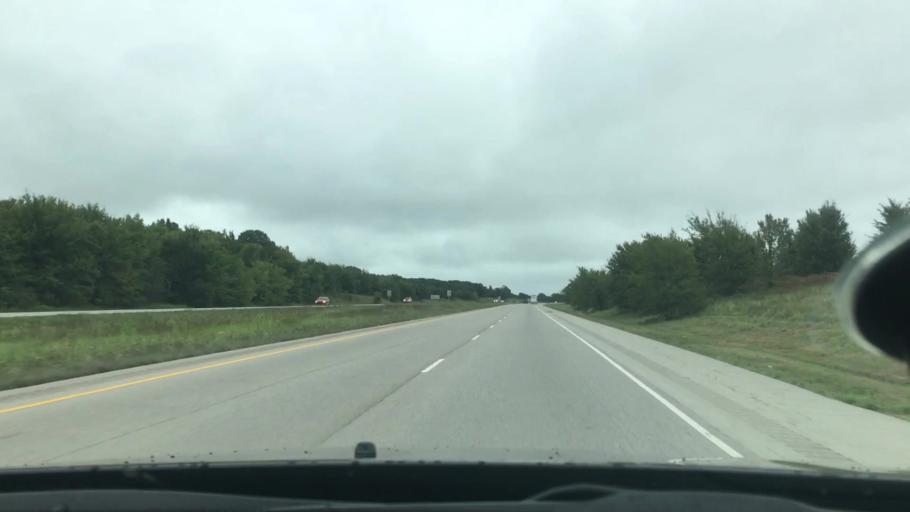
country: US
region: Oklahoma
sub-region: Okfuskee County
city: Okemah
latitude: 35.3969
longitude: -96.3944
